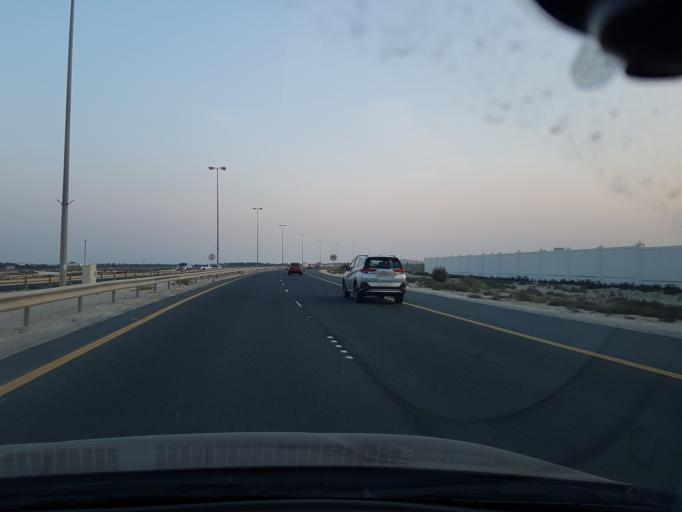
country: BH
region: Central Governorate
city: Dar Kulayb
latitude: 26.0345
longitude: 50.4997
